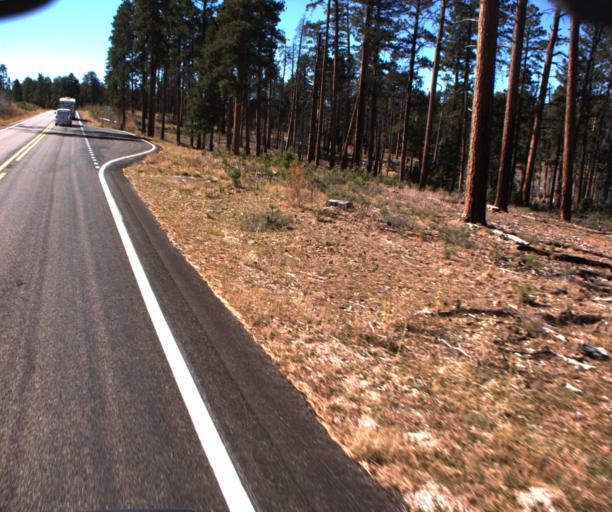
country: US
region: Arizona
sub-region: Coconino County
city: Fredonia
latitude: 36.6344
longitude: -112.1720
